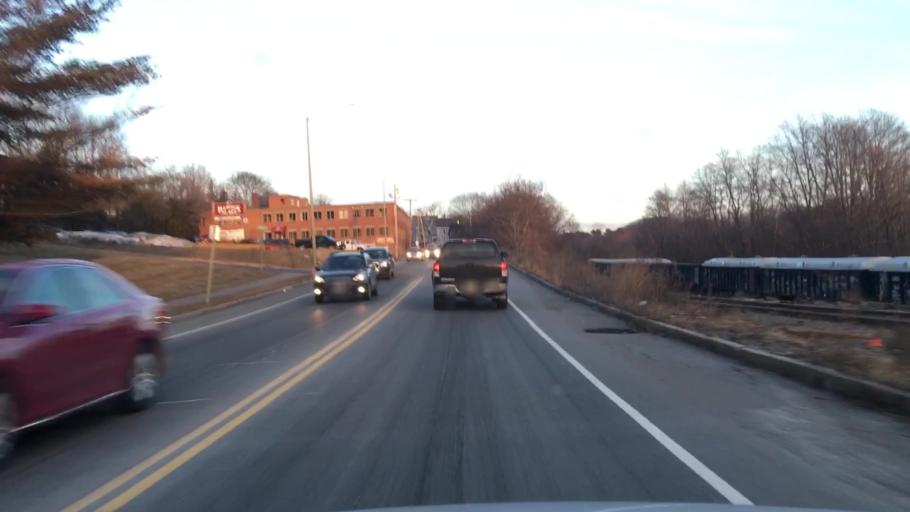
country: US
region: Maine
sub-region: Penobscot County
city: Brewer
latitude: 44.8024
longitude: -68.7620
